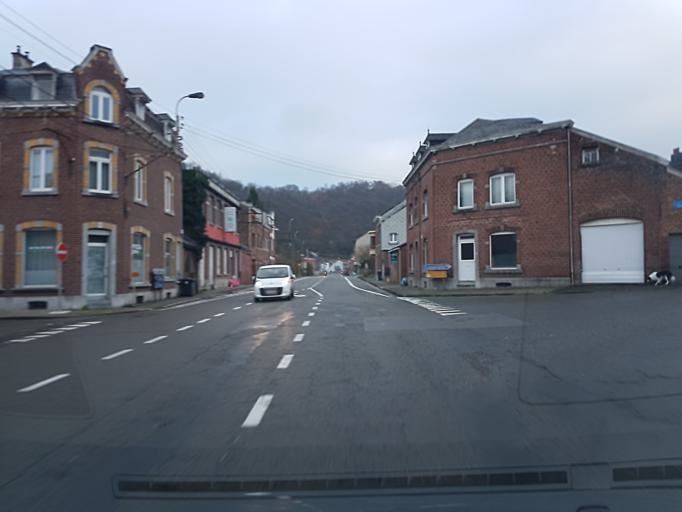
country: BE
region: Wallonia
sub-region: Province de Liege
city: Olne
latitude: 50.5720
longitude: 5.7397
